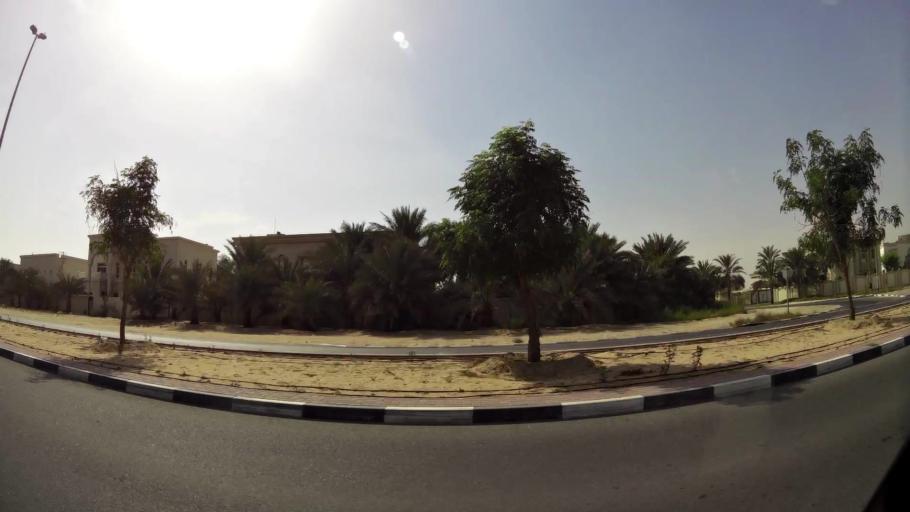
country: AE
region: Ash Shariqah
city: Sharjah
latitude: 25.2426
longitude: 55.4283
